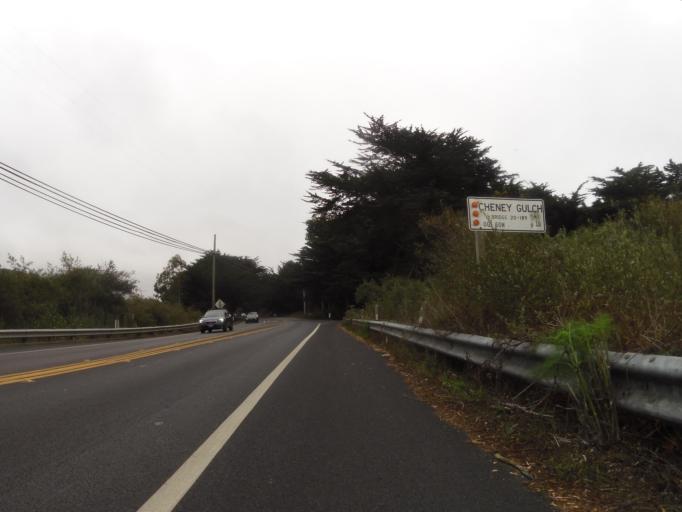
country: US
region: California
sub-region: Sonoma County
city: Bodega Bay
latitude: 38.3200
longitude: -123.0342
